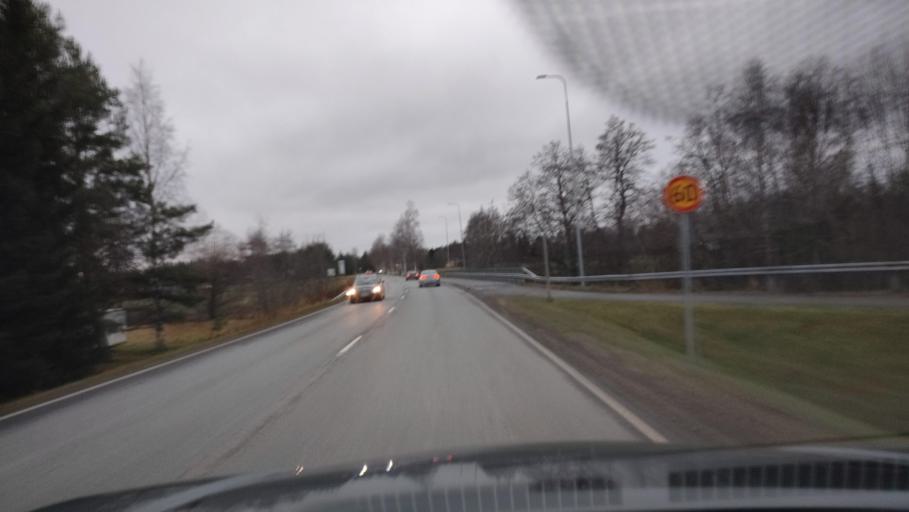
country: FI
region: Southern Ostrobothnia
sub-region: Suupohja
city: Kauhajoki
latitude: 62.4181
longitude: 22.1904
